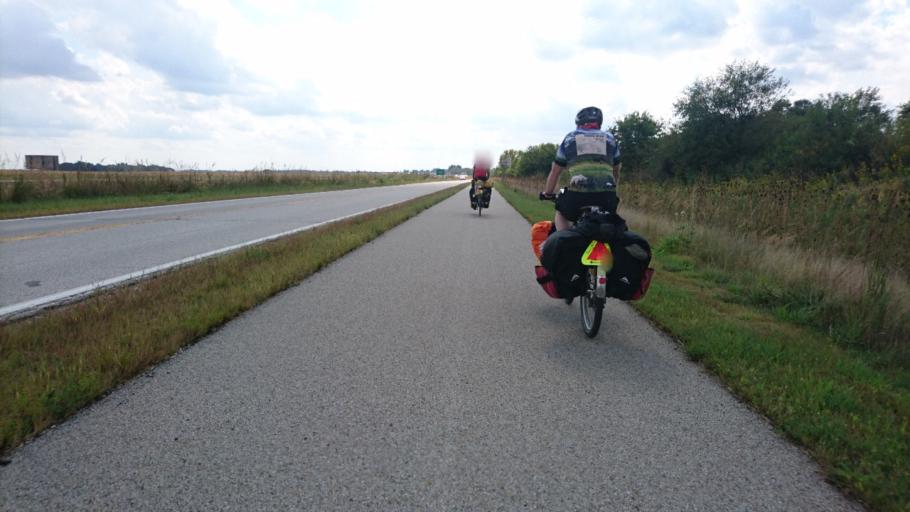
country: US
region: Illinois
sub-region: McLean County
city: Bloomington
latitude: 40.4253
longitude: -89.0401
